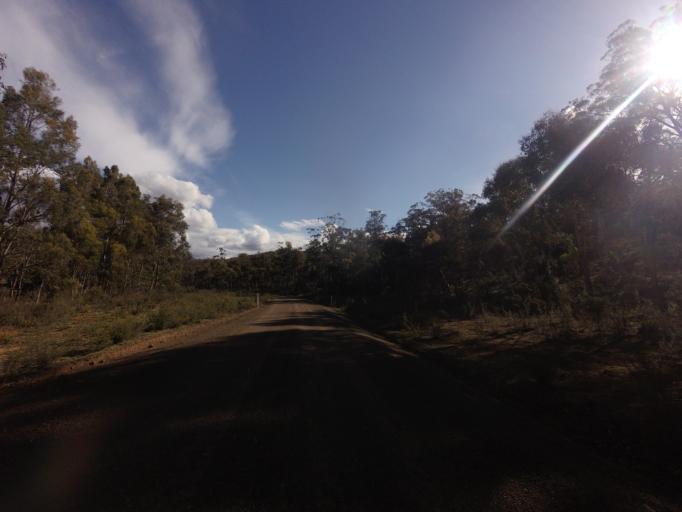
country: AU
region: Tasmania
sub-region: Break O'Day
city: St Helens
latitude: -41.8475
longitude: 148.0112
